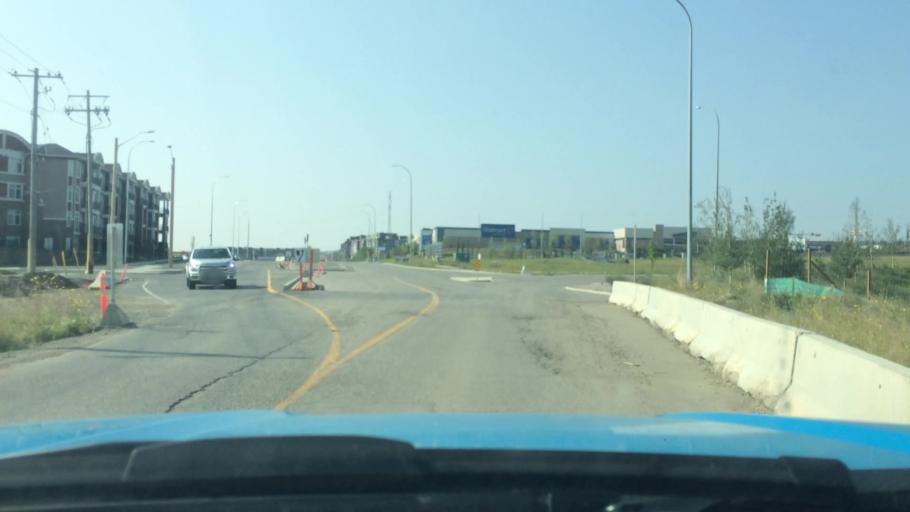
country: CA
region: Alberta
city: Calgary
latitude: 51.1730
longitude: -114.1412
